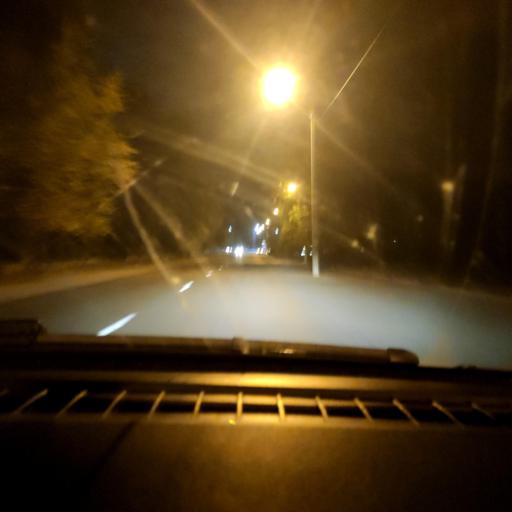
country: RU
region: Voronezj
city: Podgornoye
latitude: 51.7383
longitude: 39.1783
